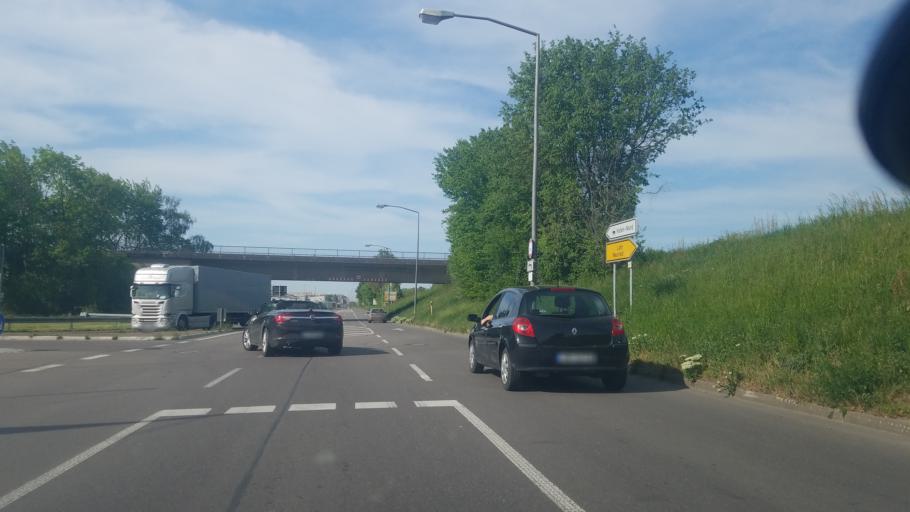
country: DE
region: Baden-Wuerttemberg
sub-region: Freiburg Region
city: Kehl
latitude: 48.5807
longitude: 7.8223
